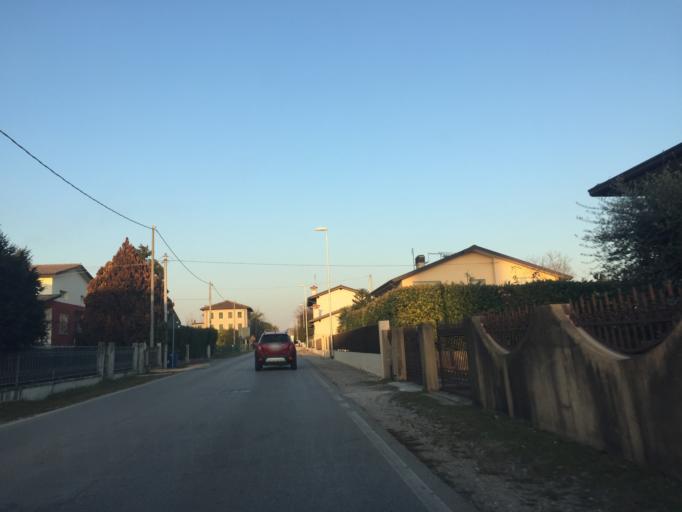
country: IT
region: Friuli Venezia Giulia
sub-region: Provincia di Pordenone
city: Vigonovo-Fontanafredda
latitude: 45.9911
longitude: 12.5490
